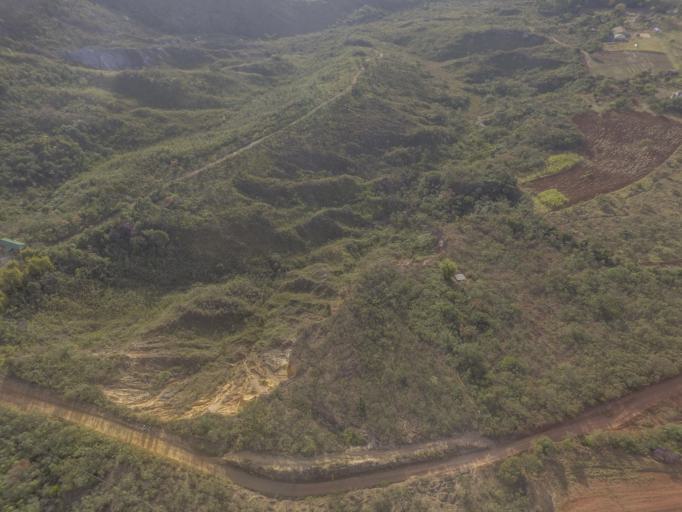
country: BR
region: Minas Gerais
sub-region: Tiradentes
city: Tiradentes
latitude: -21.0586
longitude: -44.1005
